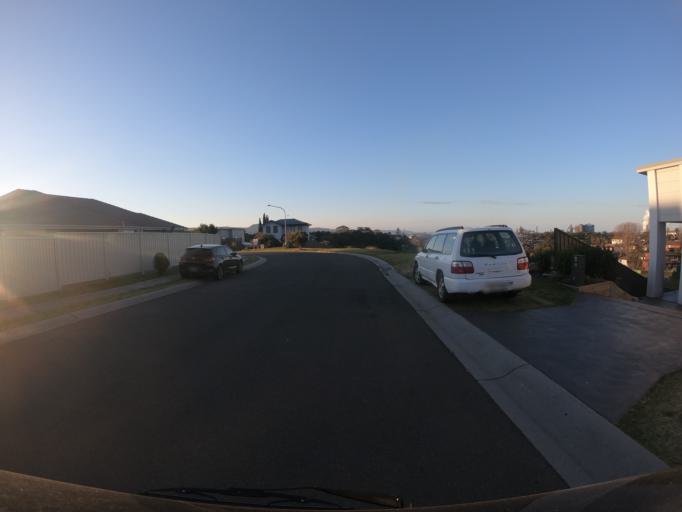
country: AU
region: New South Wales
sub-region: Wollongong
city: Lake Heights
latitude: -34.4778
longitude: 150.8690
